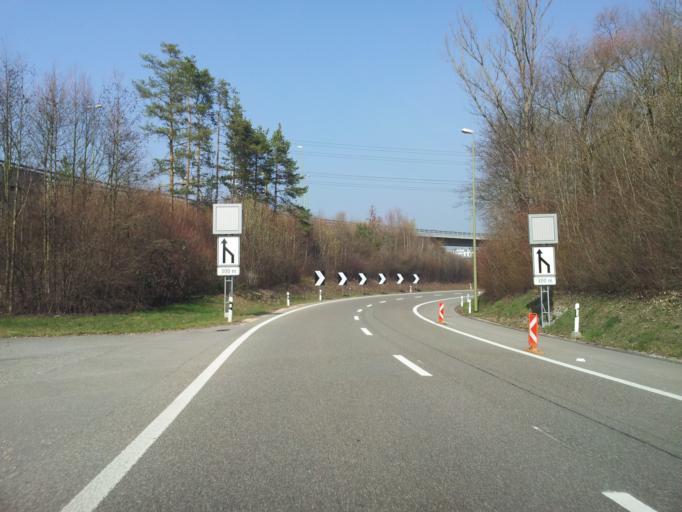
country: CH
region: Zurich
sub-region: Bezirk Buelach
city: Wallisellen / Wallisellen-Ost
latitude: 47.4058
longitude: 8.5997
